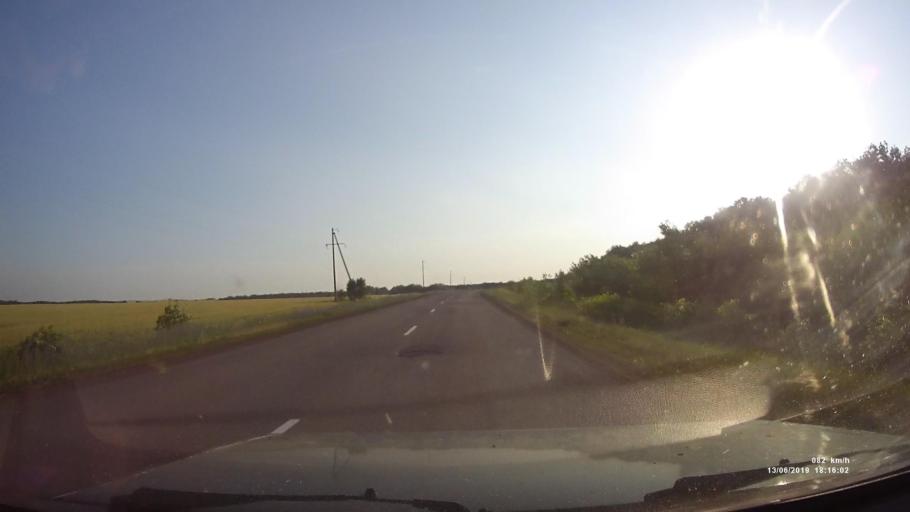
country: RU
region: Rostov
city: Kazanskaya
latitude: 49.9286
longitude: 41.3465
